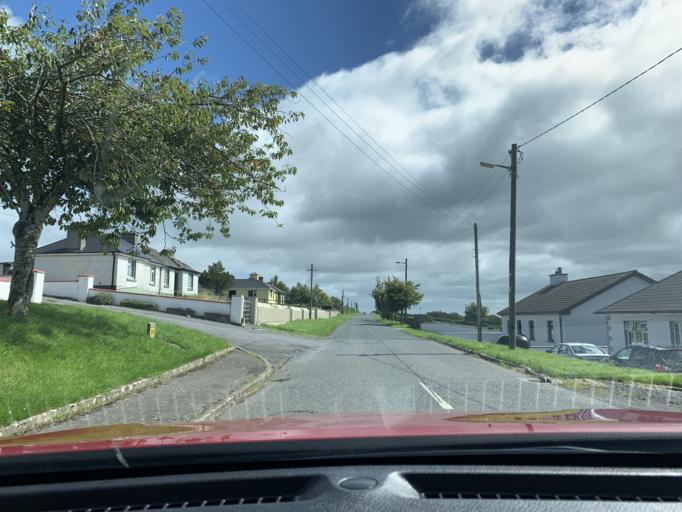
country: IE
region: Connaught
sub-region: County Leitrim
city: Carrick-on-Shannon
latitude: 53.8460
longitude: -8.1870
